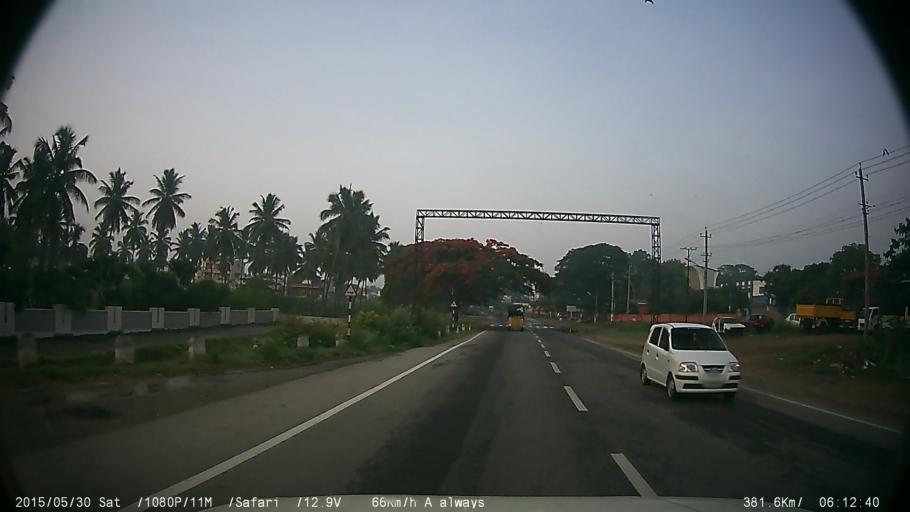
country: IN
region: Karnataka
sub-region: Mysore
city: Mysore
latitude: 12.3399
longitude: 76.6581
